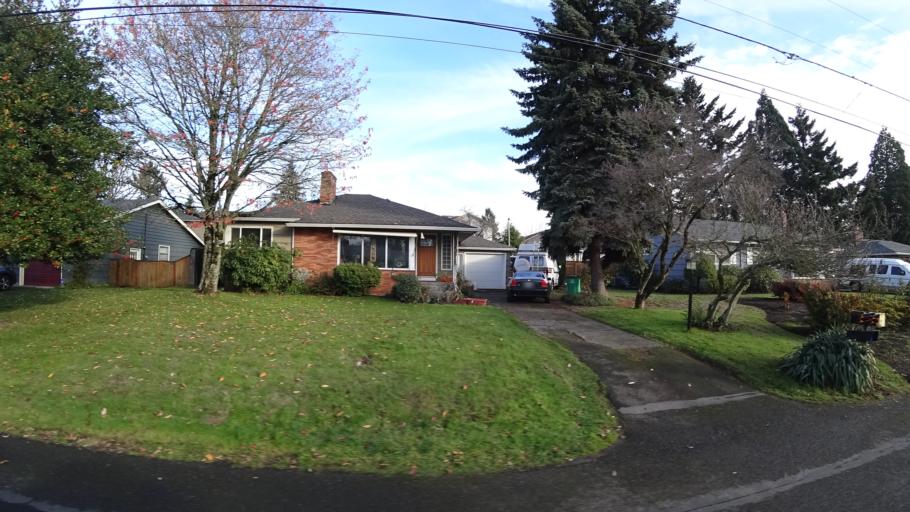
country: US
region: Oregon
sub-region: Multnomah County
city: Lents
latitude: 45.5252
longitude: -122.5280
